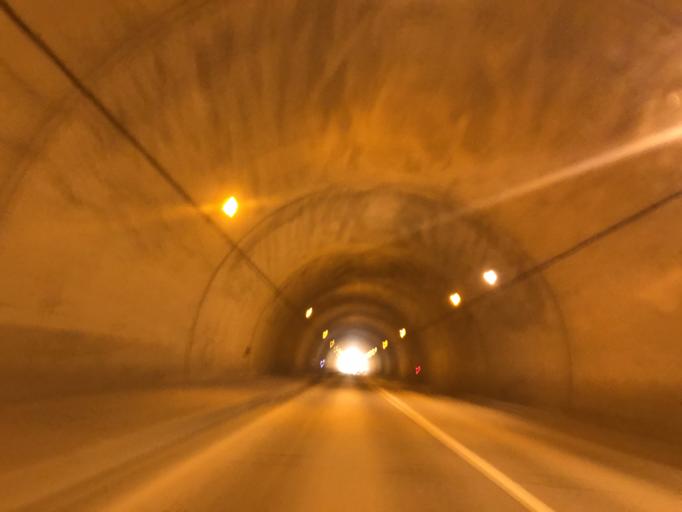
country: JP
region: Akita
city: Yokotemachi
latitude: 39.3555
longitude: 140.7624
